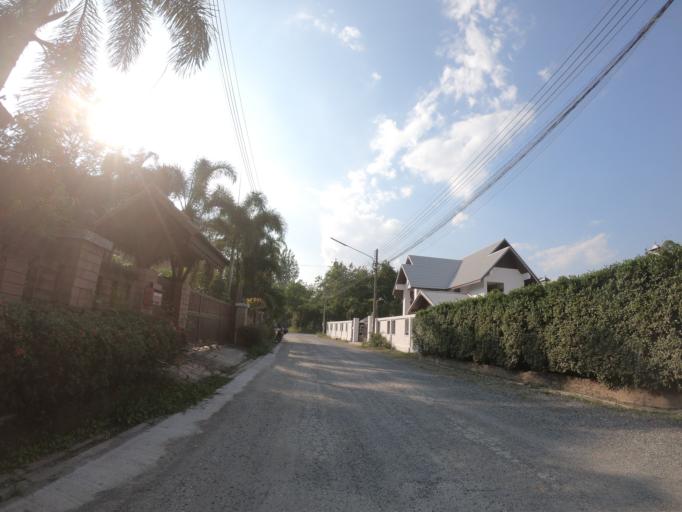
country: TH
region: Chiang Mai
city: San Sai
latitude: 18.8312
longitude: 99.0083
